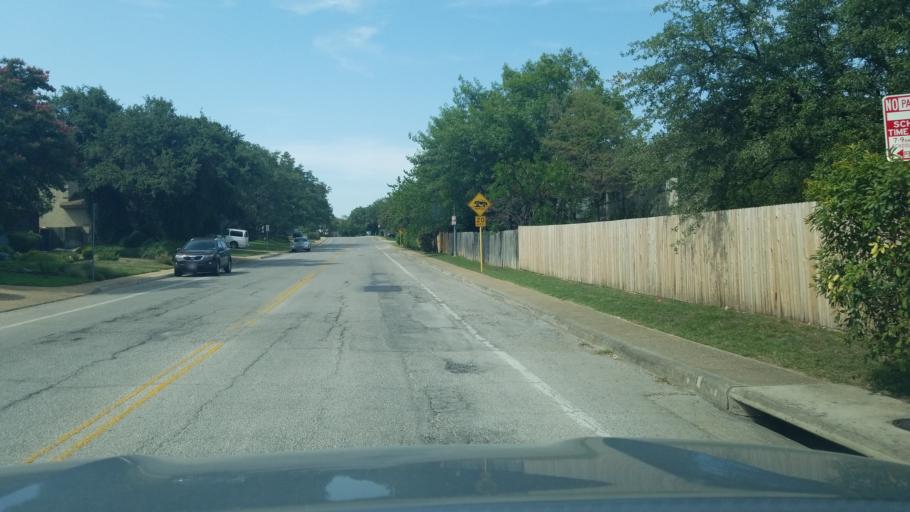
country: US
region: Texas
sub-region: Bexar County
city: Hollywood Park
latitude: 29.6274
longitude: -98.4880
